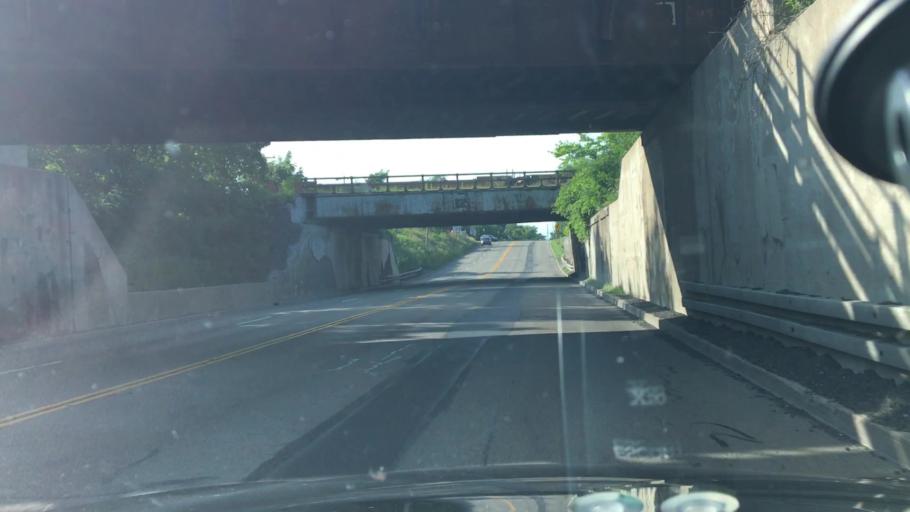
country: US
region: New York
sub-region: Erie County
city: Wanakah
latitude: 42.7646
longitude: -78.8642
